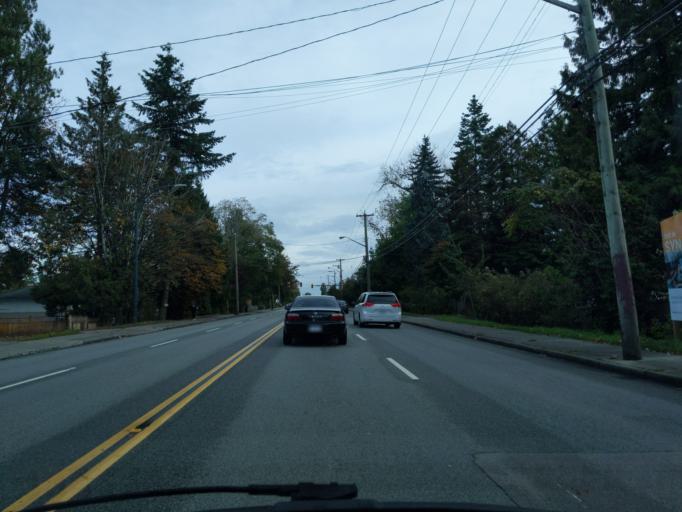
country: CA
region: British Columbia
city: New Westminster
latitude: 49.1988
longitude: -122.8392
